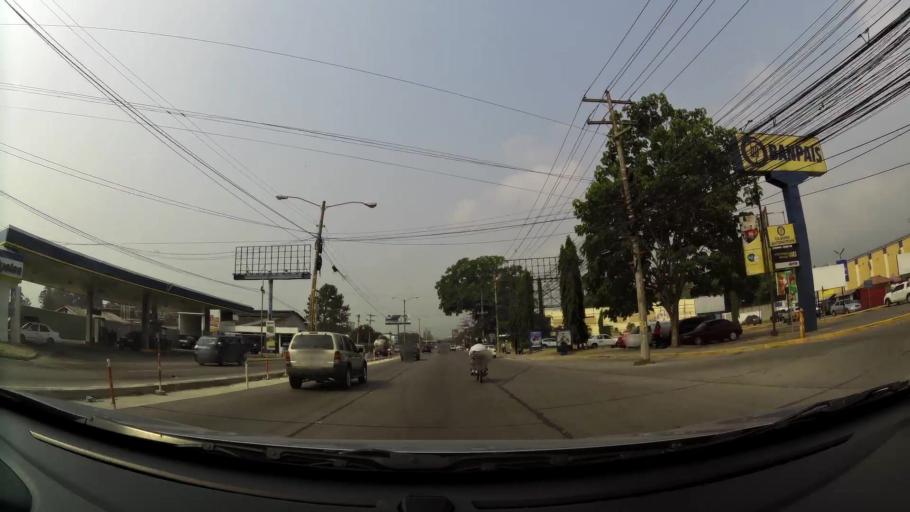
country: HN
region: Cortes
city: San Pedro Sula
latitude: 15.5337
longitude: -88.0190
